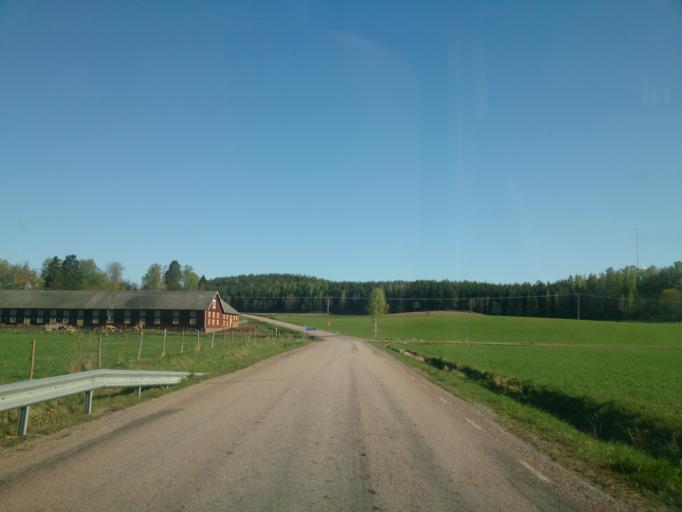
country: SE
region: OEstergoetland
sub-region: Linkopings Kommun
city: Ljungsbro
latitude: 58.5543
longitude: 15.5210
